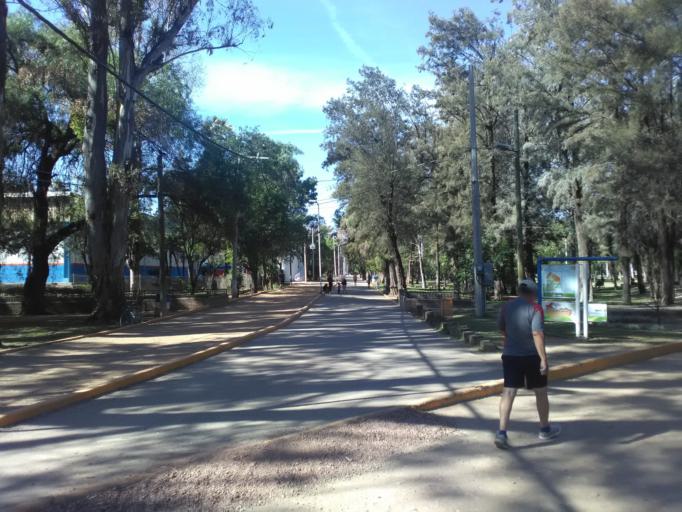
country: MX
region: Durango
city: Victoria de Durango
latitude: 24.0281
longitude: -104.6852
